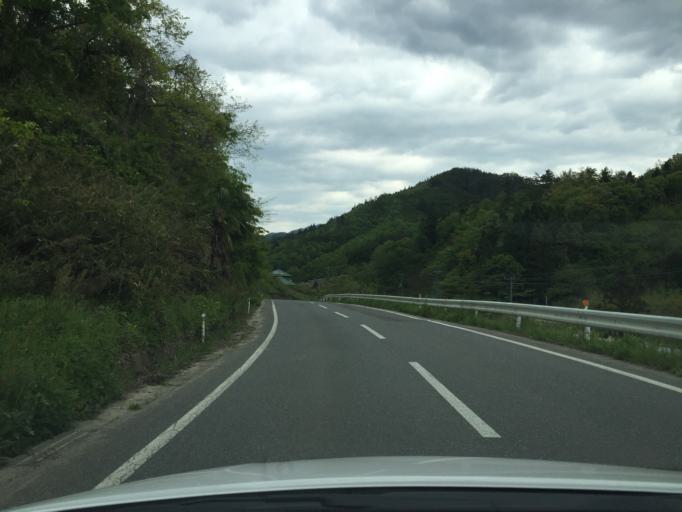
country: JP
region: Fukushima
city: Yanagawamachi-saiwaicho
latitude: 37.7510
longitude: 140.6418
